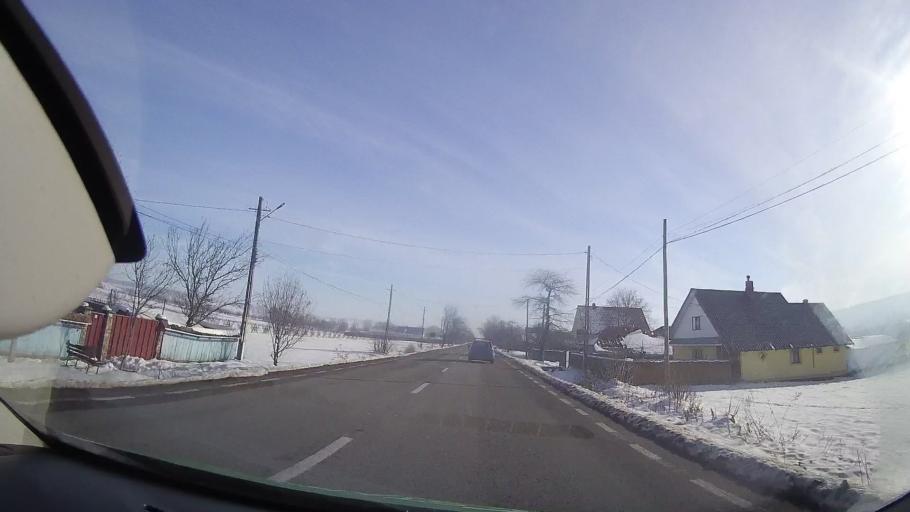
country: RO
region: Neamt
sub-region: Comuna Negresti
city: Negresti
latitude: 47.0600
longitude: 26.3860
